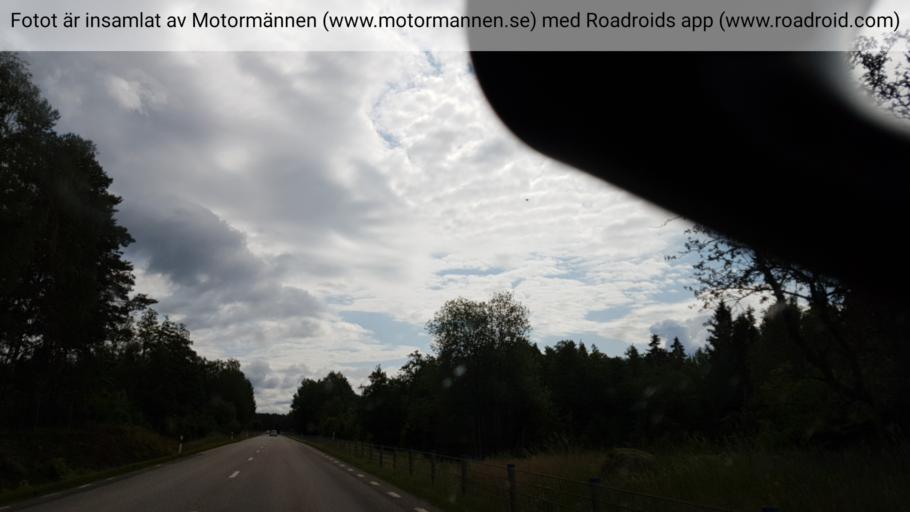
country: SE
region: Vaestra Goetaland
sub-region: Vara Kommun
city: Kvanum
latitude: 58.2143
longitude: 13.2225
